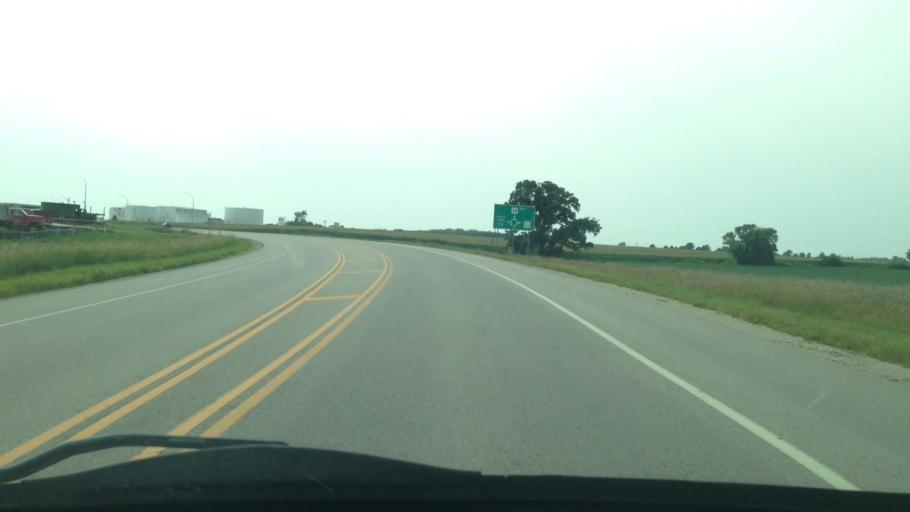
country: US
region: Minnesota
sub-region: Olmsted County
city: Eyota
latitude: 43.9983
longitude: -92.2426
